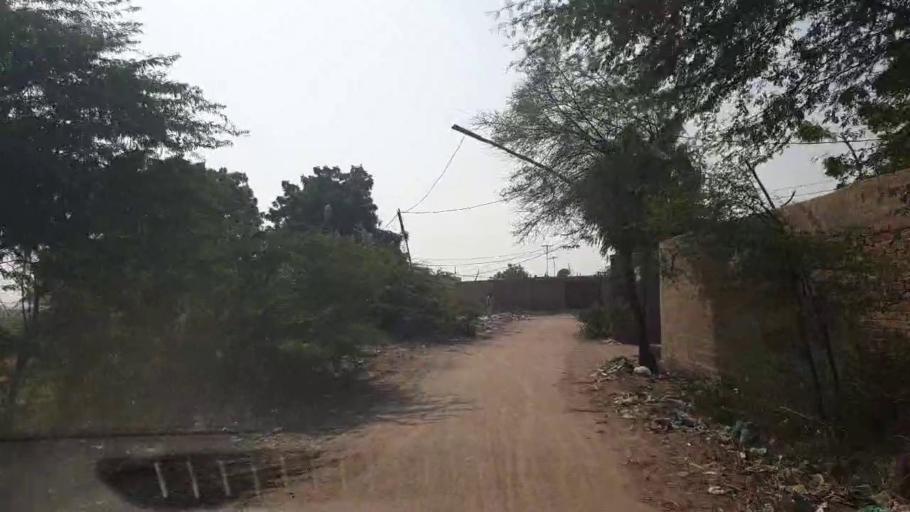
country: PK
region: Sindh
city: Kotri
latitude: 25.3370
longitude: 68.2817
